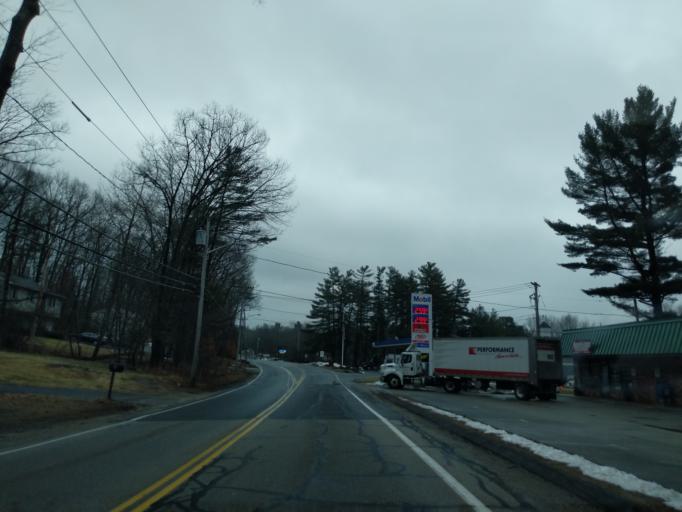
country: US
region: Massachusetts
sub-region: Worcester County
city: Webster
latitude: 42.0546
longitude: -71.8406
